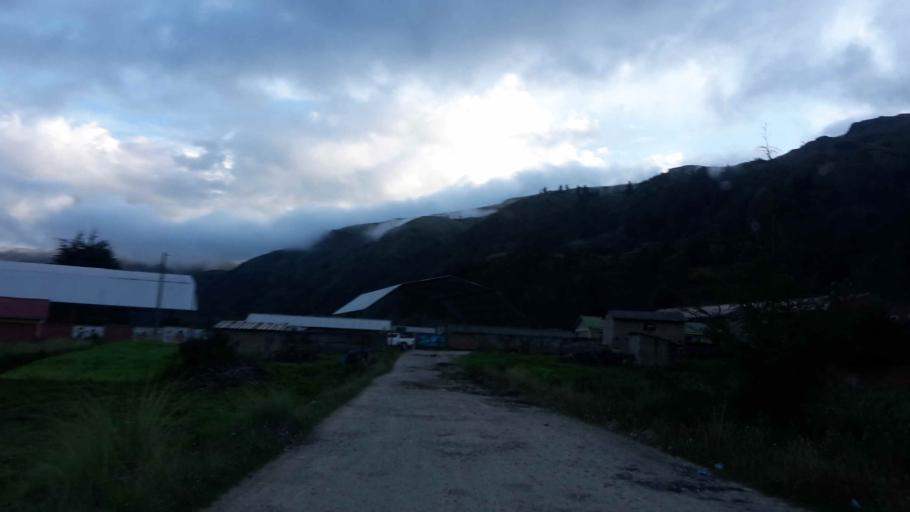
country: BO
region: Cochabamba
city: Colomi
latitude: -17.2734
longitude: -65.9246
